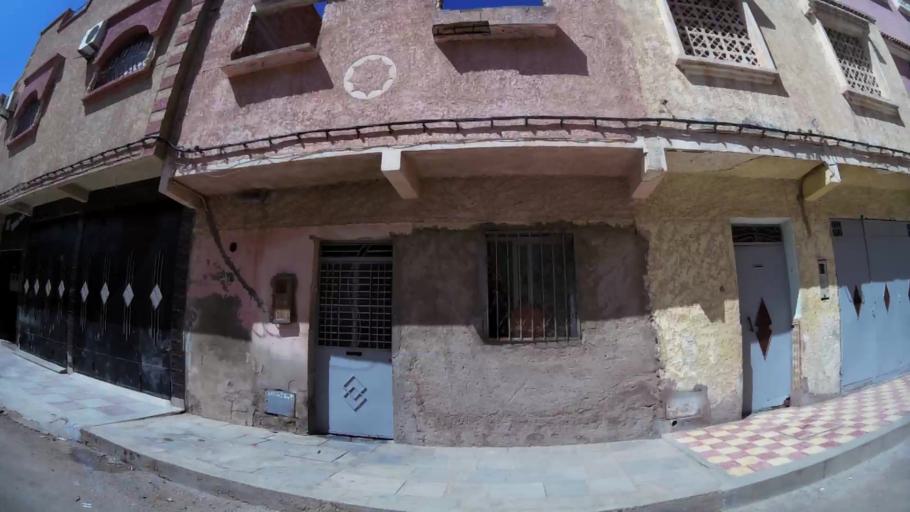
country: MA
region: Oriental
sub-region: Oujda-Angad
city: Oujda
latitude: 34.6704
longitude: -1.9436
